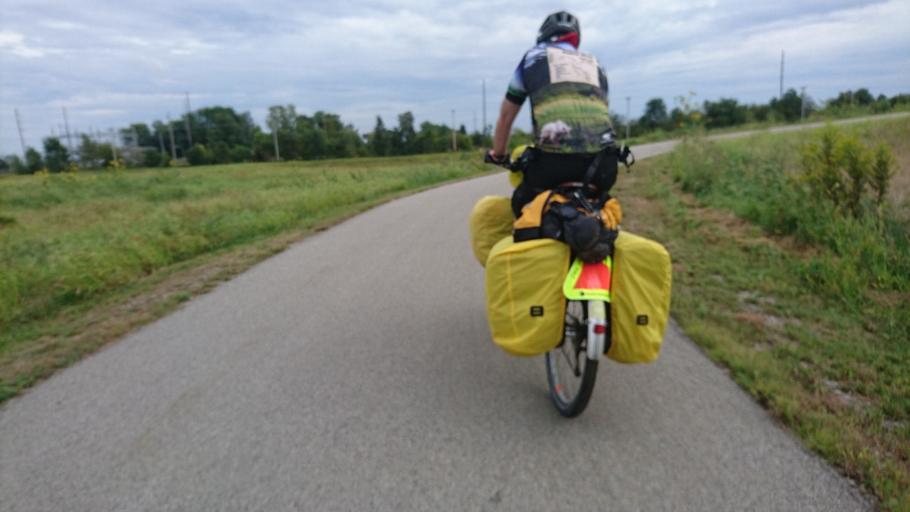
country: US
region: Illinois
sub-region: Sangamon County
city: Southern View
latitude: 39.7454
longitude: -89.6699
